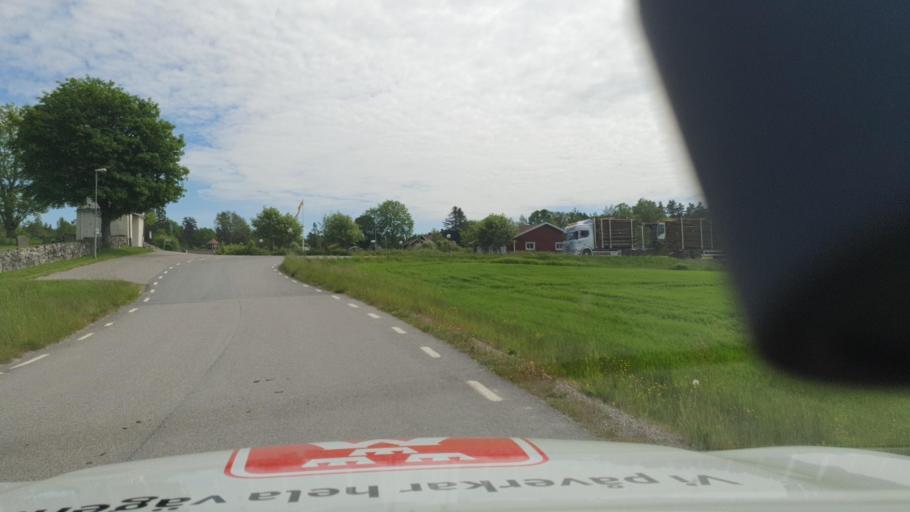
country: SE
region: Vaestra Goetaland
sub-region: Vanersborgs Kommun
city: Vargon
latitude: 58.2856
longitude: 12.5179
